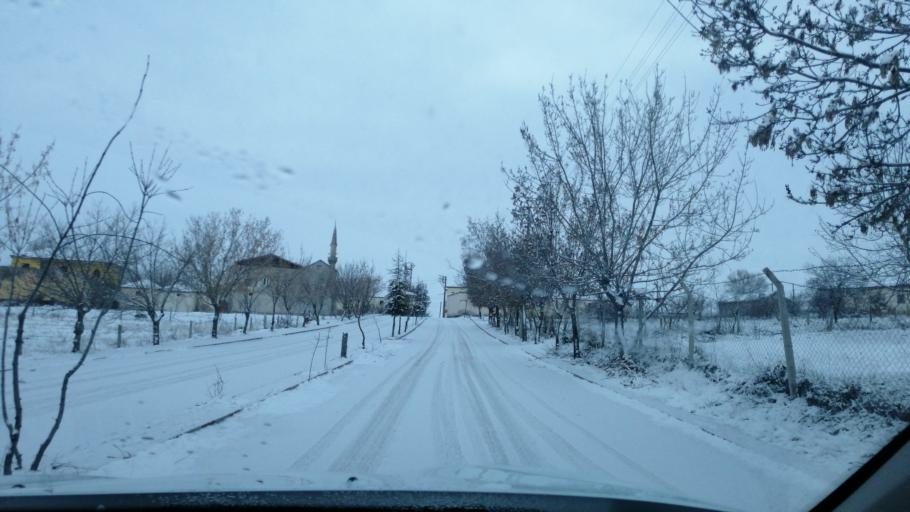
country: TR
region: Aksaray
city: Agacoren
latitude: 38.9285
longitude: 33.9551
